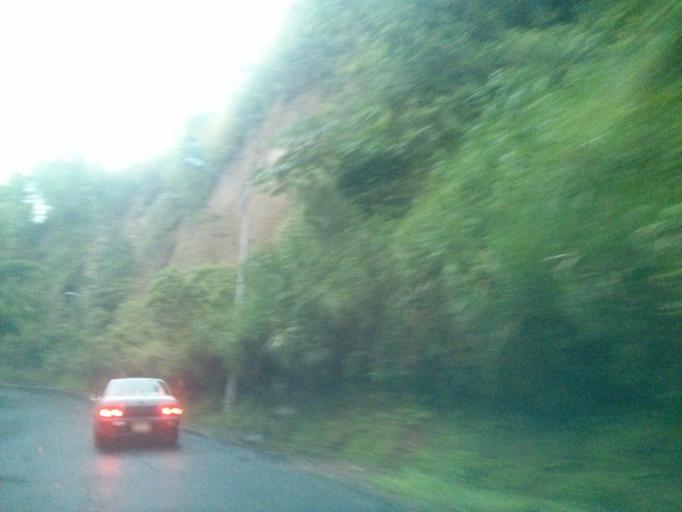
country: CR
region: Alajuela
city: Sabanilla
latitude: 10.0530
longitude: -84.2038
